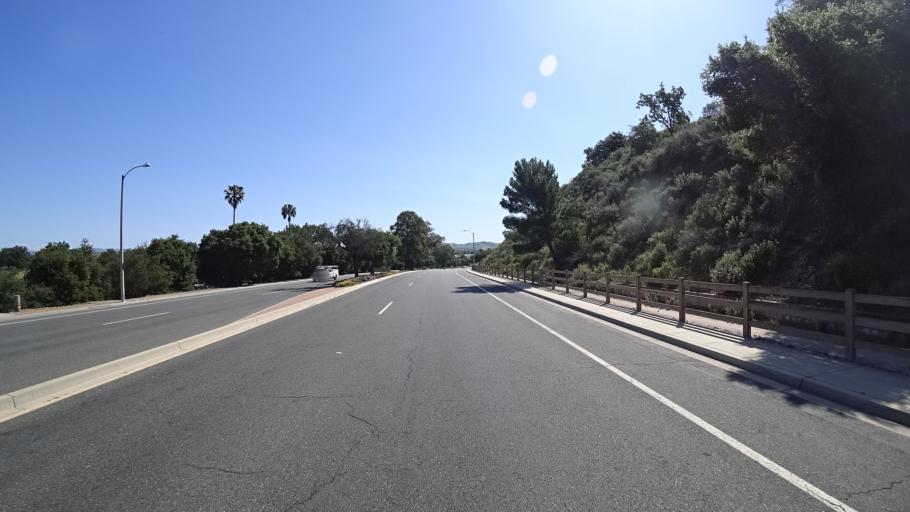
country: US
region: California
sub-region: Ventura County
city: Casa Conejo
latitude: 34.1765
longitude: -118.9162
